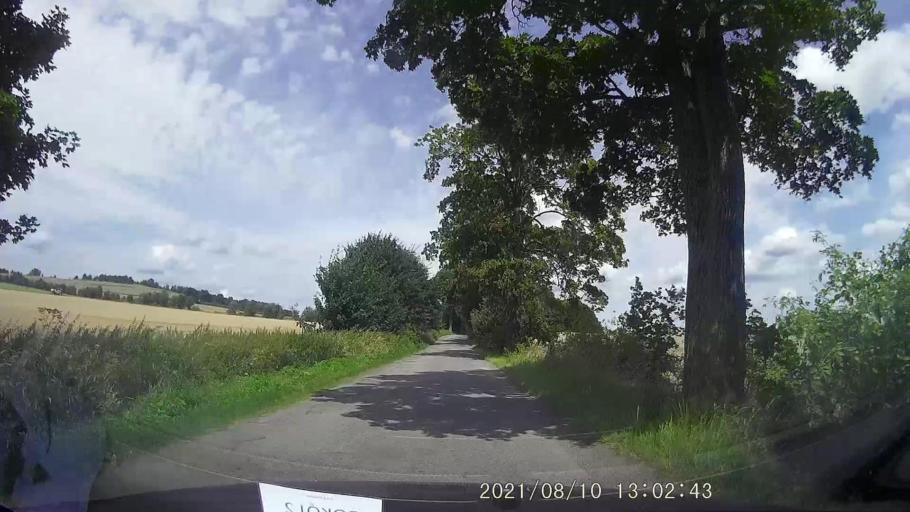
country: PL
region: Lower Silesian Voivodeship
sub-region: Powiat klodzki
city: Bozkow
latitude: 50.4663
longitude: 16.5590
